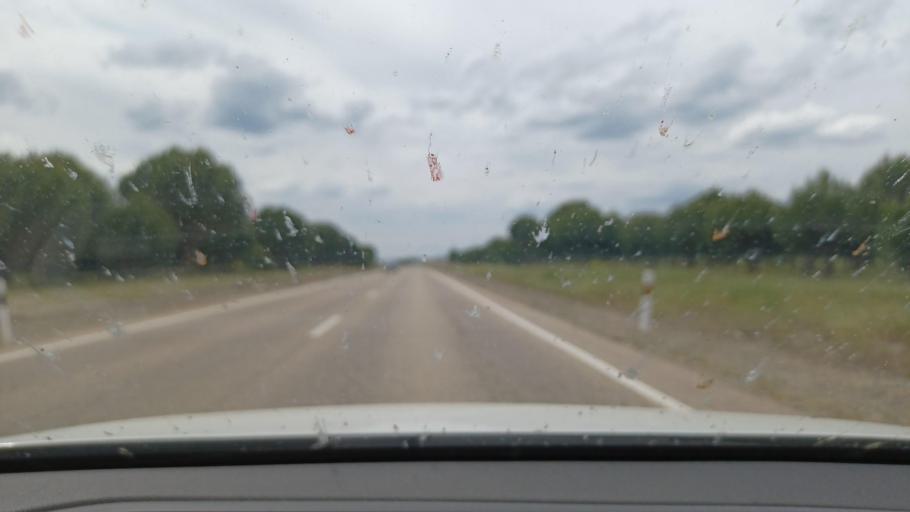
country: ES
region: Castille and Leon
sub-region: Provincia de Segovia
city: Frumales
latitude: 41.3828
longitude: -4.2236
